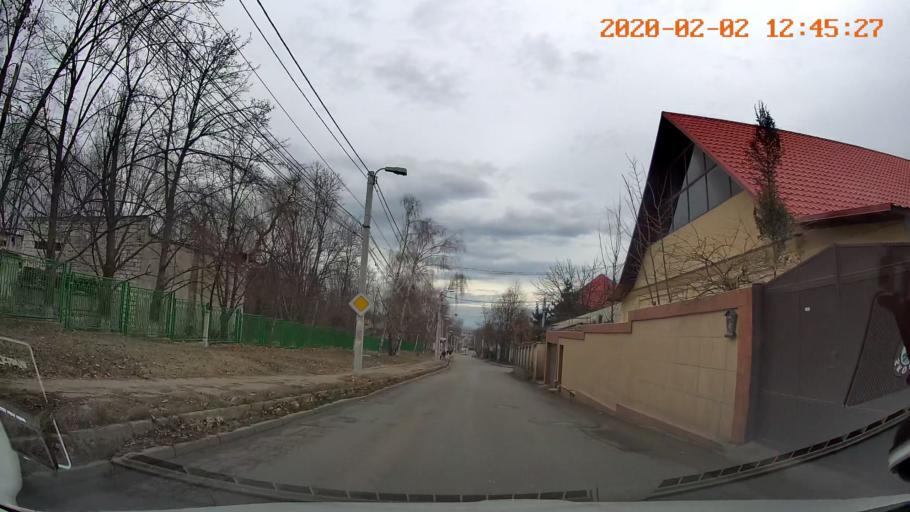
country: MD
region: Chisinau
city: Chisinau
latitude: 47.0052
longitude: 28.8135
